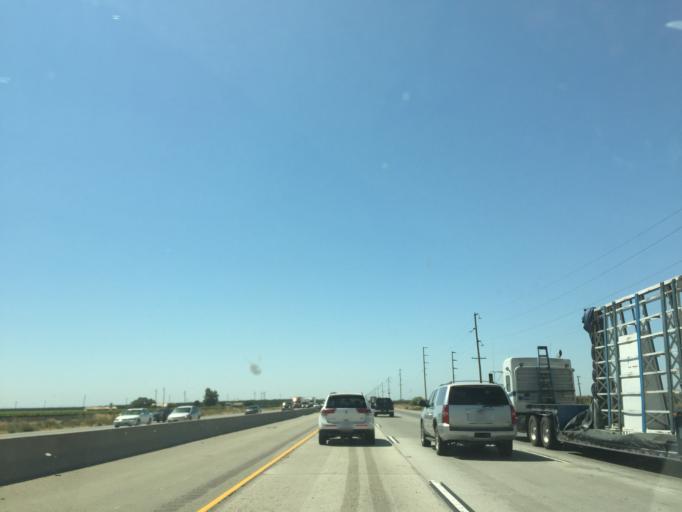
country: US
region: California
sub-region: Kern County
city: Greenacres
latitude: 35.4690
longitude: -119.1235
